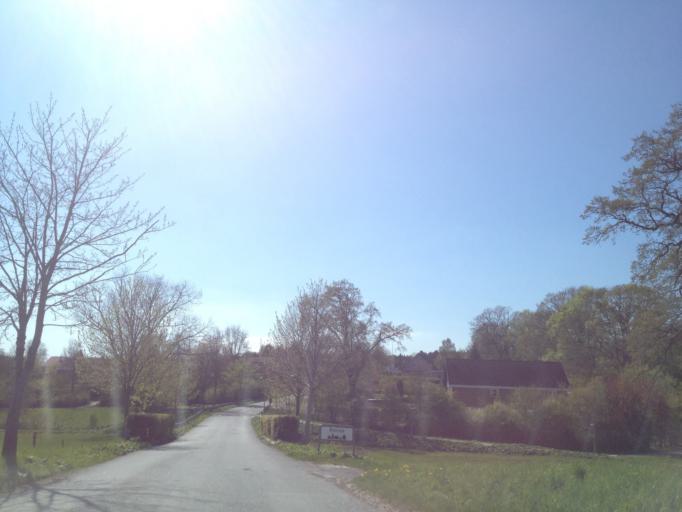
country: DK
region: Zealand
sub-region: Koge Kommune
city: Borup
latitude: 55.5079
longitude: 11.9846
